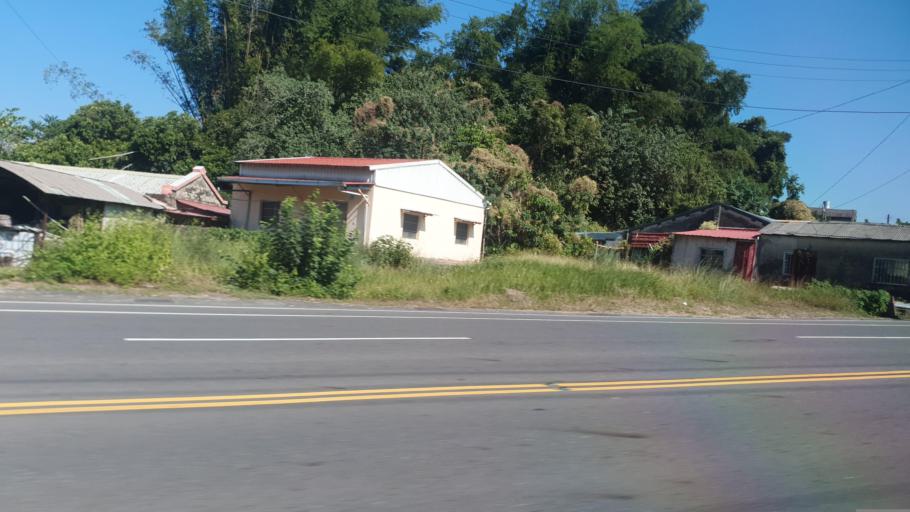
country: TW
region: Taiwan
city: Yujing
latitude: 23.0646
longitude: 120.3836
